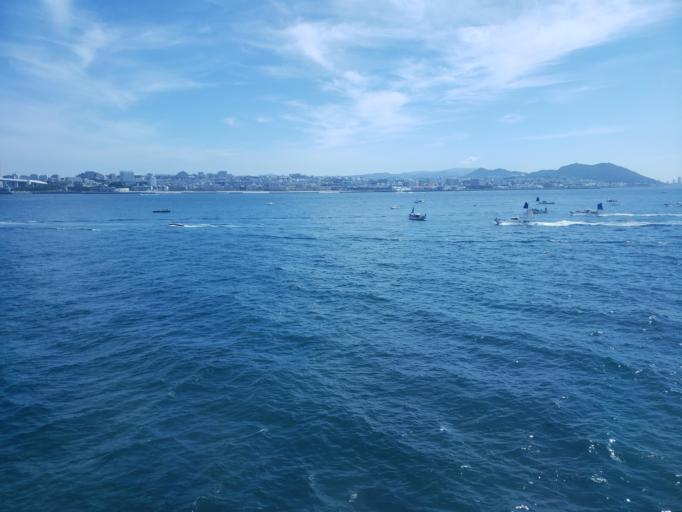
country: JP
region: Hyogo
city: Akashi
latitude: 34.6127
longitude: 135.0333
